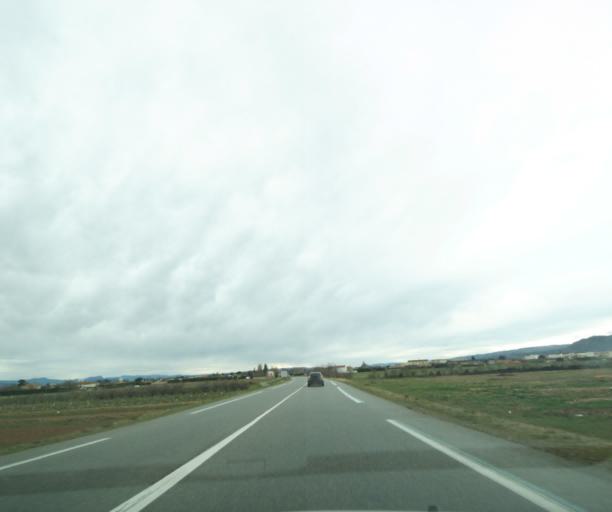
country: FR
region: Rhone-Alpes
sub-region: Departement de la Drome
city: Bourg-les-Valence
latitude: 44.9641
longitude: 4.9102
